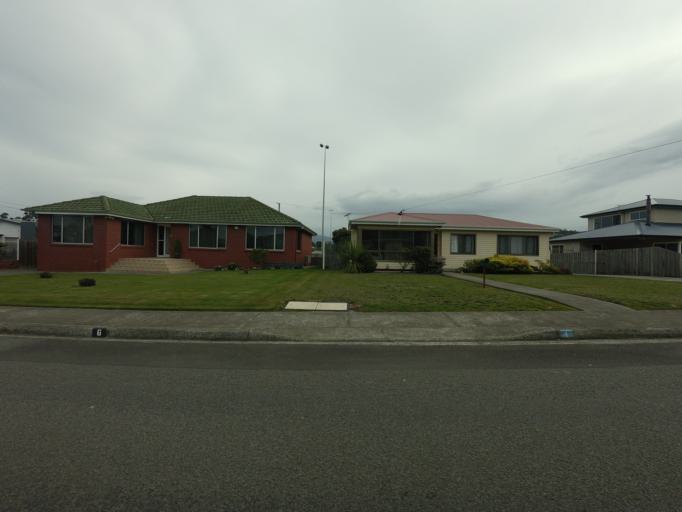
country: AU
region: Tasmania
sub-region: Clarence
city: Howrah
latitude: -42.8786
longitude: 147.3965
